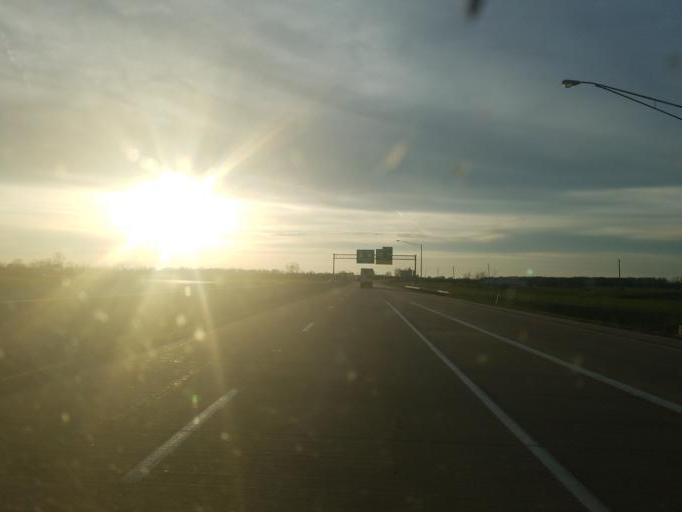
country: US
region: Ohio
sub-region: Wood County
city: Luckey
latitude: 41.4881
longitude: -83.4546
